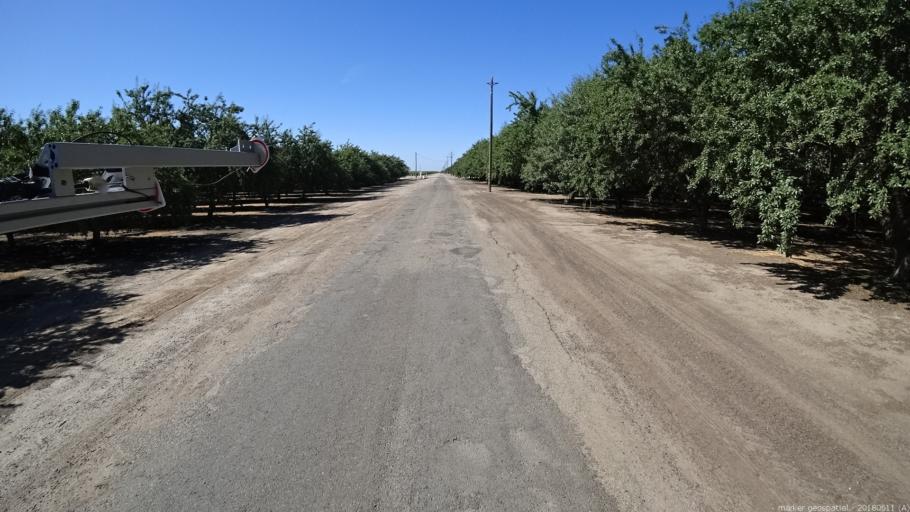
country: US
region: California
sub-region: Madera County
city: Madera
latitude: 36.9468
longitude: -120.1466
